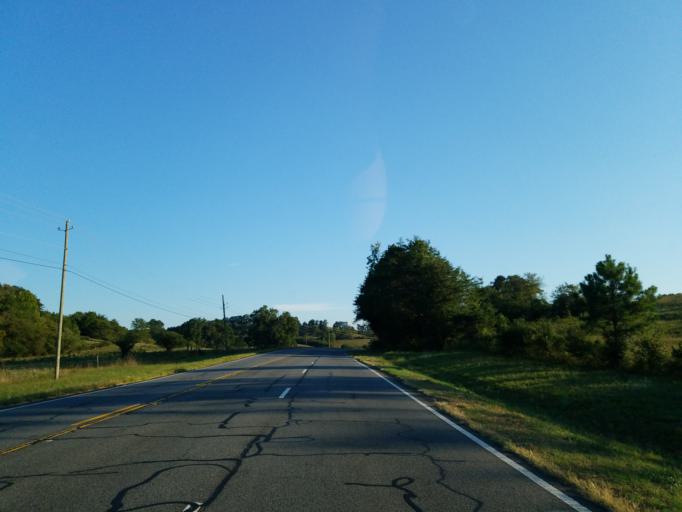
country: US
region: Georgia
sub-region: Bartow County
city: Rydal
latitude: 34.3906
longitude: -84.7063
